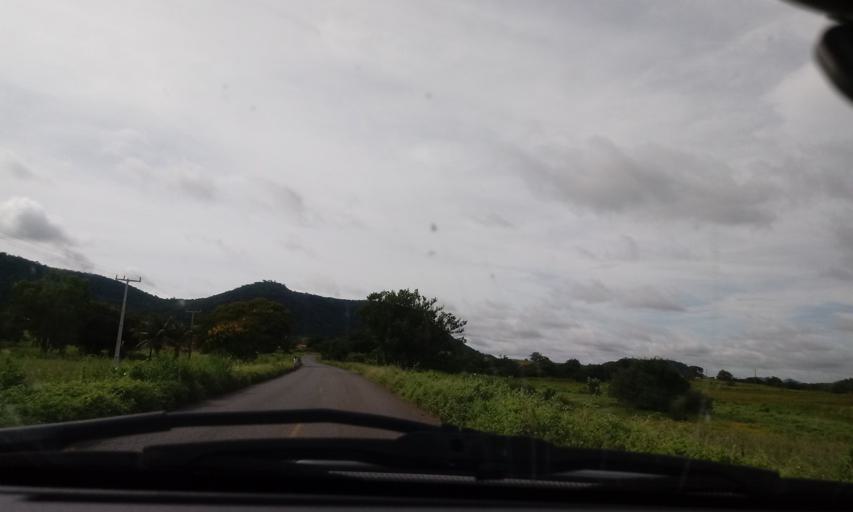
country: BR
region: Bahia
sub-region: Guanambi
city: Guanambi
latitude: -14.1173
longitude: -42.8583
